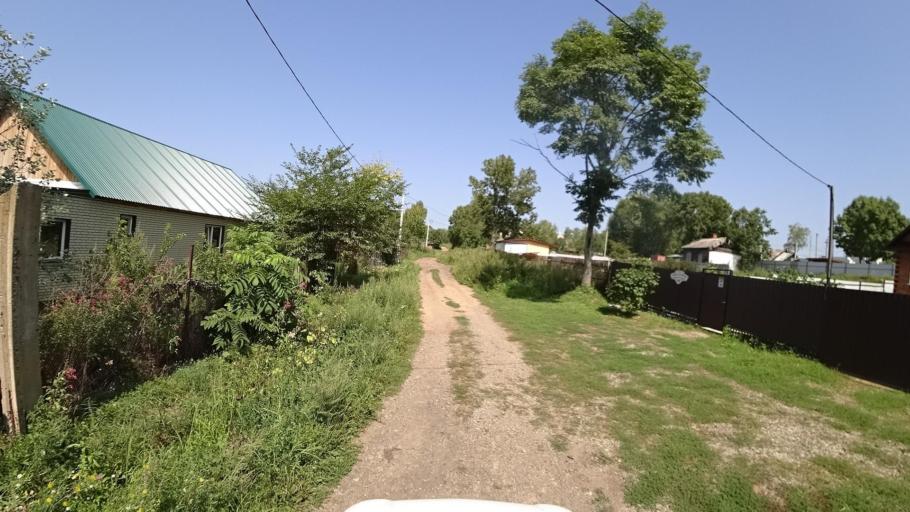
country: RU
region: Khabarovsk Krai
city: Khor
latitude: 47.9622
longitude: 135.1145
